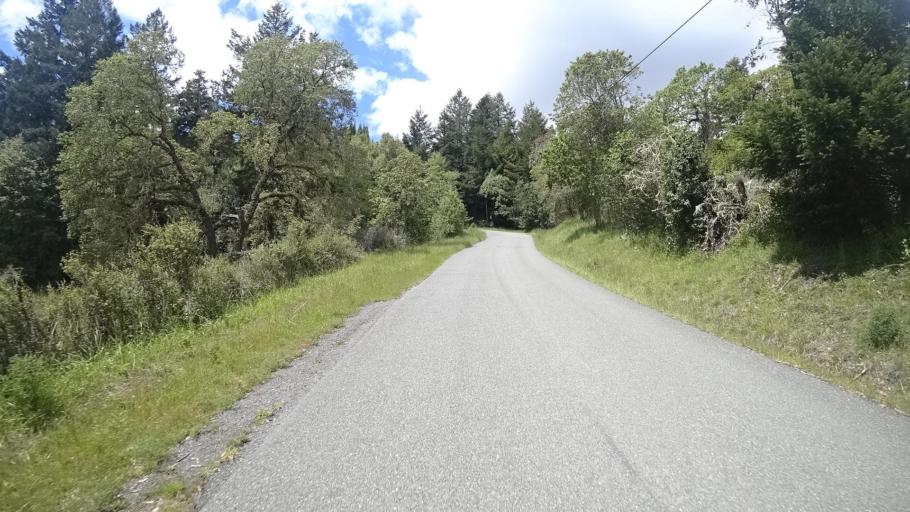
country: US
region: California
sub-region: Humboldt County
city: Blue Lake
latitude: 40.8439
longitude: -123.9063
